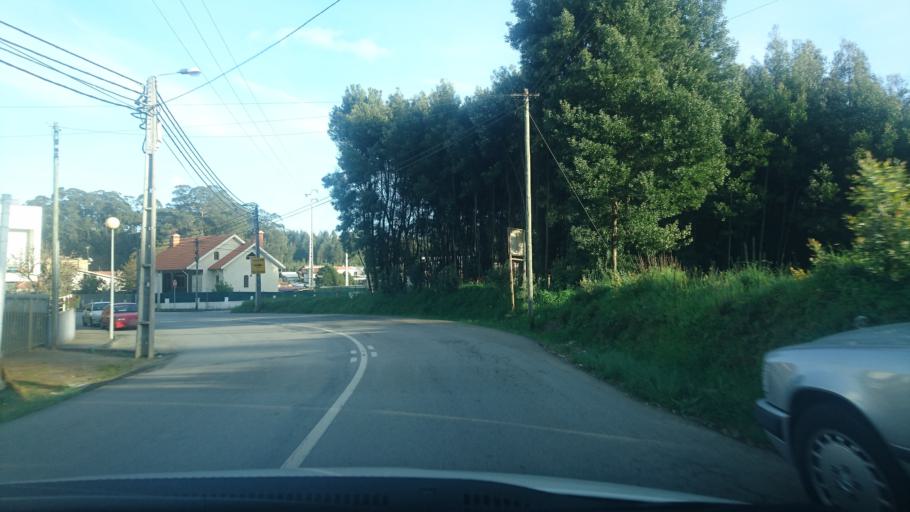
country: PT
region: Aveiro
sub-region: Santa Maria da Feira
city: Nogueira da Regedoura
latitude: 40.9994
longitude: -8.5999
